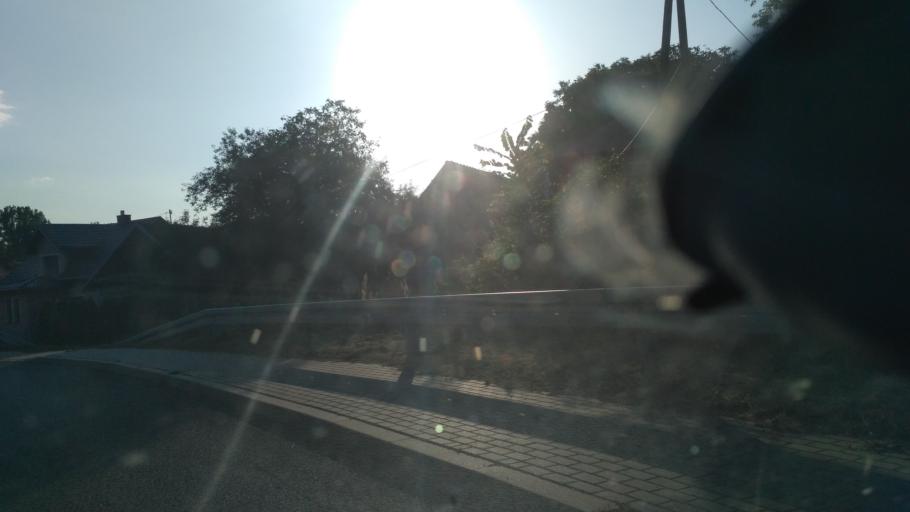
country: PL
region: Subcarpathian Voivodeship
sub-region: Powiat lezajski
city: Kurylowka
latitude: 50.2982
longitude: 22.4611
